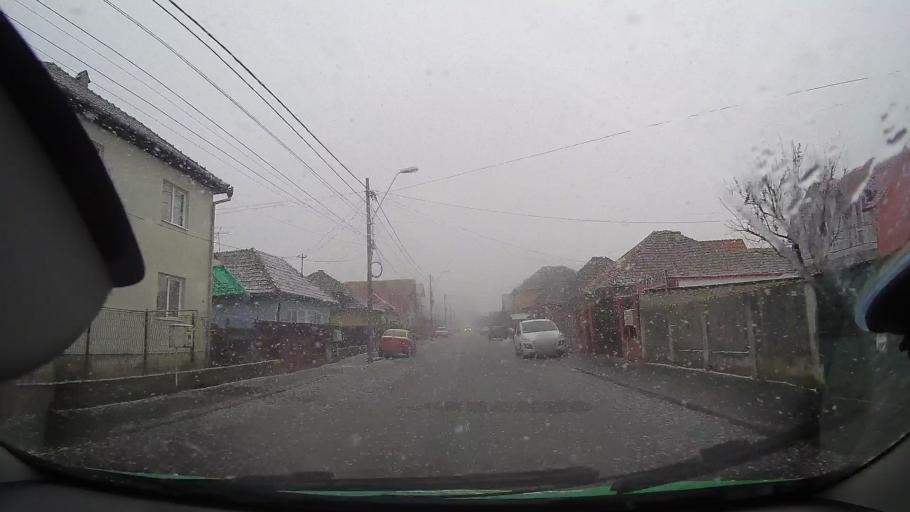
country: RO
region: Sibiu
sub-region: Municipiul Medias
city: Medias
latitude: 46.1693
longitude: 24.3763
